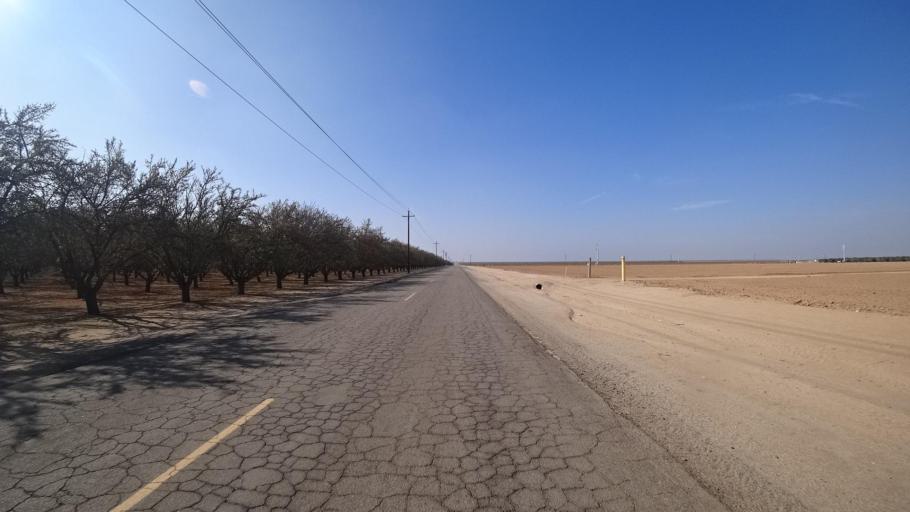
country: US
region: California
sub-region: Kern County
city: Shafter
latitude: 35.5298
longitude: -119.1387
